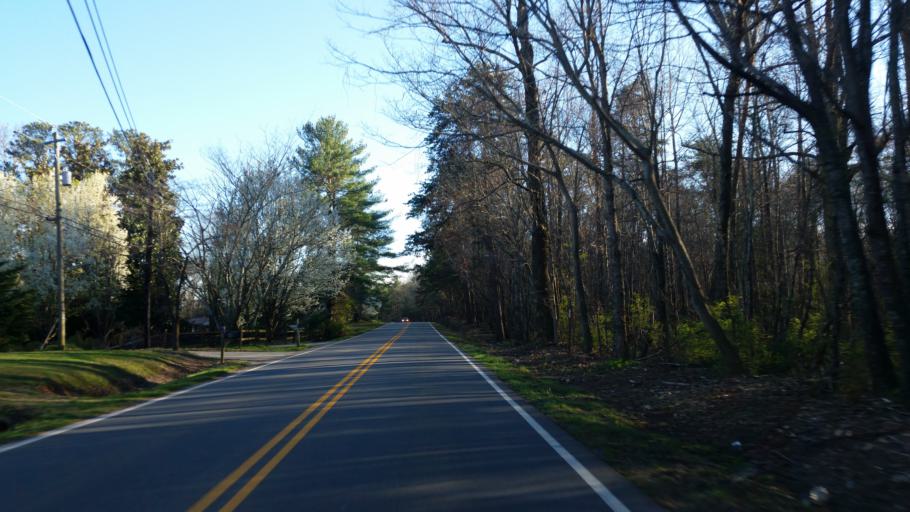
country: US
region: Georgia
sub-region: Pickens County
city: Jasper
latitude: 34.4315
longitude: -84.4211
